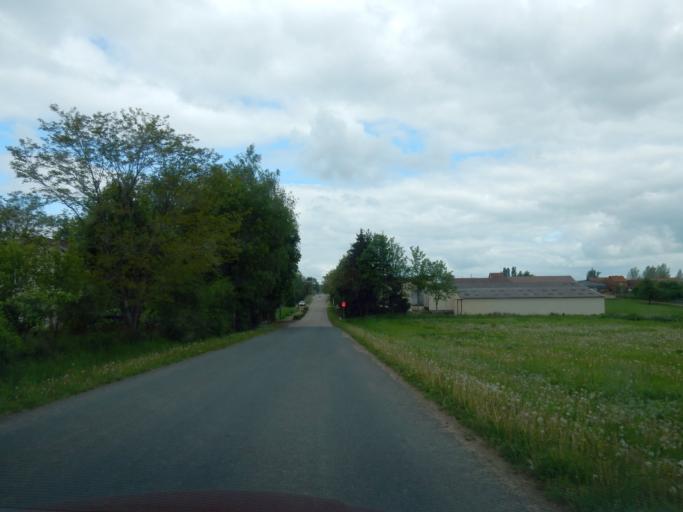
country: FR
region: Lorraine
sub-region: Departement de la Meuse
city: Verdun
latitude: 49.1987
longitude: 5.4942
